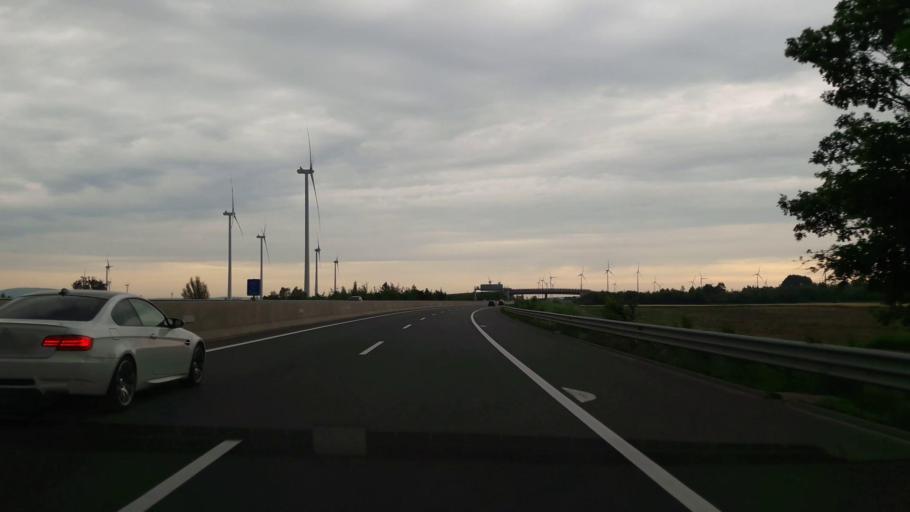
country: AT
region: Burgenland
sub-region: Politischer Bezirk Neusiedl am See
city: Parndorf
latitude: 48.0261
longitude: 16.8511
